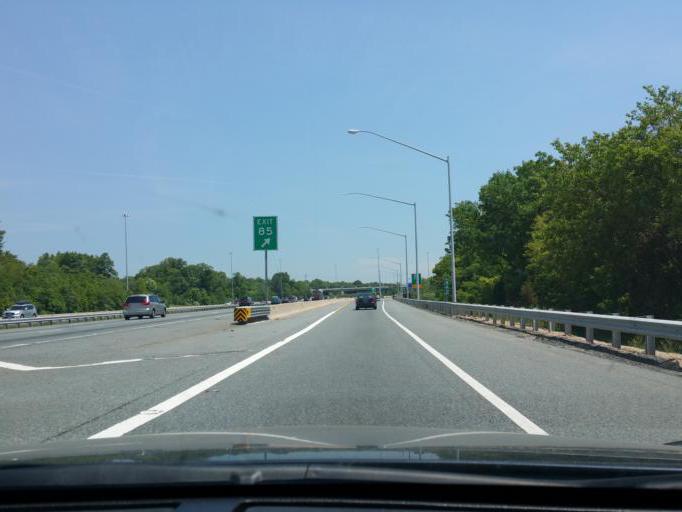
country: US
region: Maryland
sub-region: Harford County
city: Aberdeen
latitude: 39.5219
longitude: -76.1971
